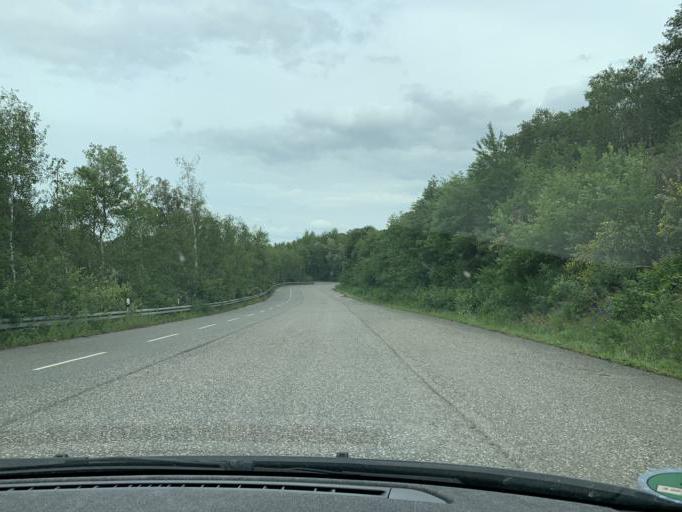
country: DE
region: North Rhine-Westphalia
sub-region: Regierungsbezirk Koln
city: Merzenich
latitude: 50.8686
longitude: 6.5155
